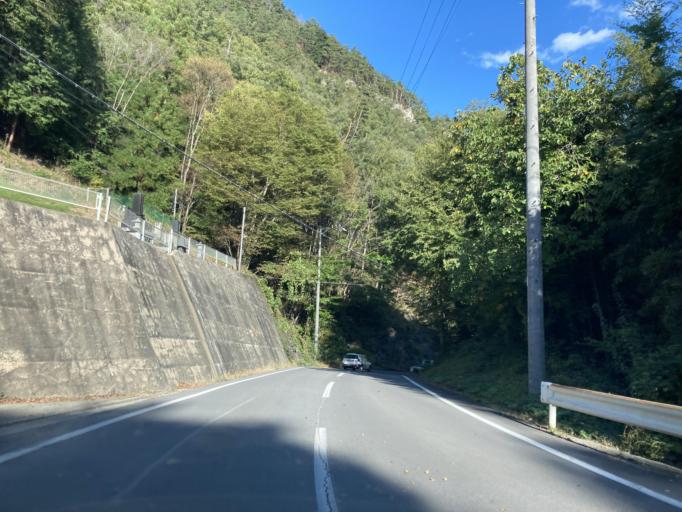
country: JP
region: Nagano
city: Omachi
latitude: 36.4668
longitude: 137.9494
